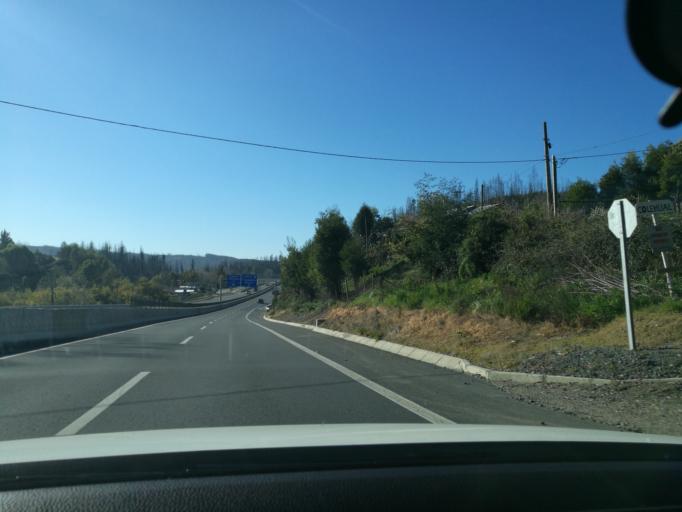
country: CL
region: Biobio
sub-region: Provincia de Concepcion
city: Chiguayante
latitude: -36.8555
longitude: -72.8927
